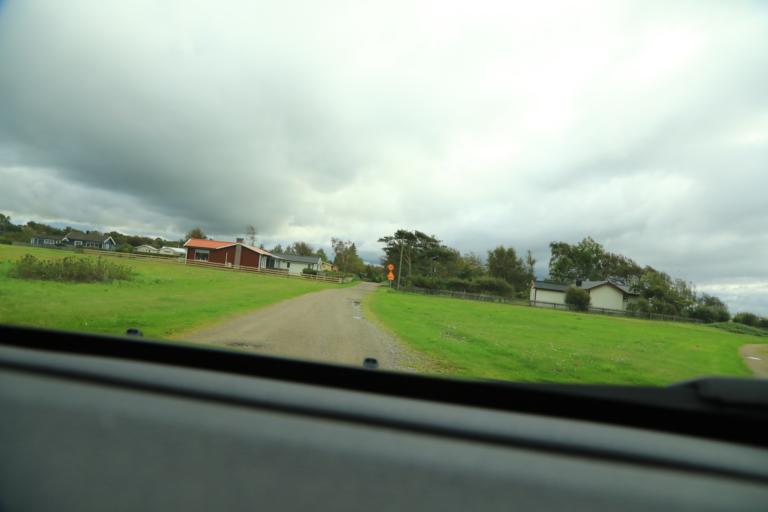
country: SE
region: Halland
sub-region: Varbergs Kommun
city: Tvaaker
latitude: 57.0122
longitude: 12.3493
